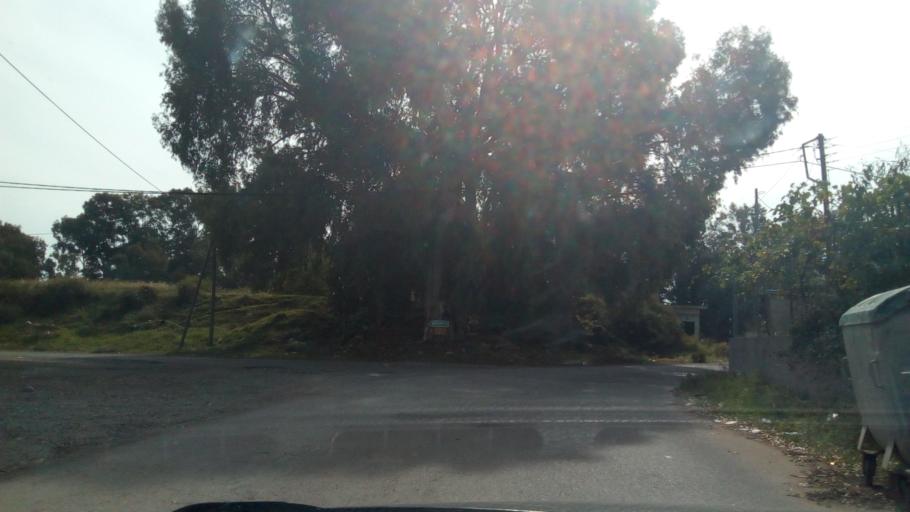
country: GR
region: West Greece
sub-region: Nomos Aitolias kai Akarnanias
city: Nafpaktos
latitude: 38.3991
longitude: 21.8679
